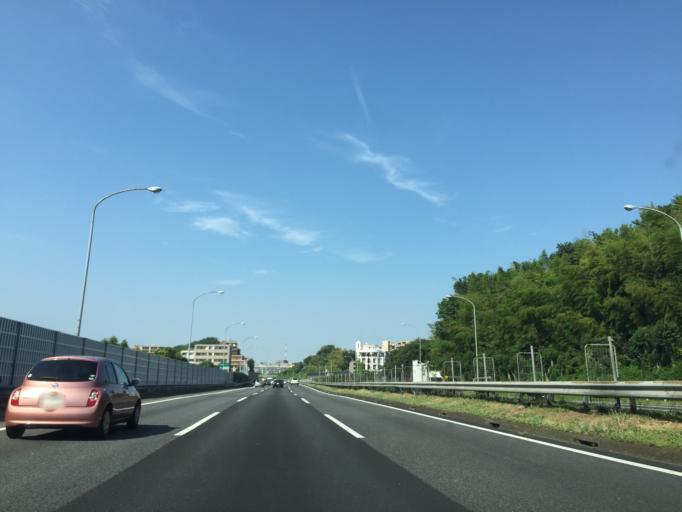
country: JP
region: Tokyo
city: Chofugaoka
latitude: 35.5608
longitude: 139.5546
